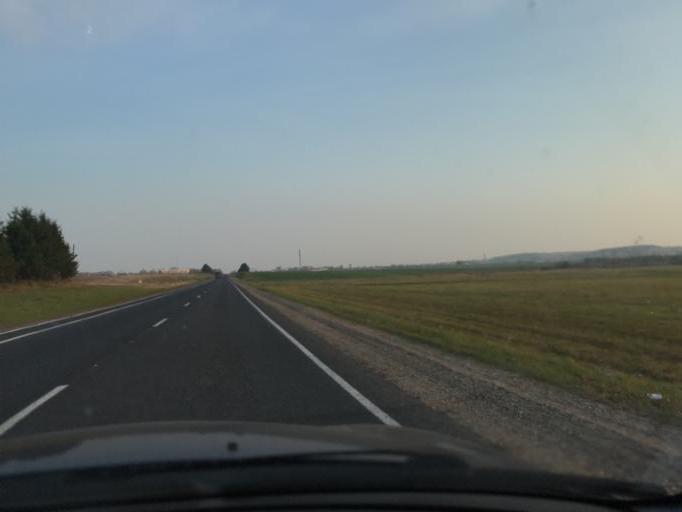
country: BY
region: Grodnenskaya
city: Karelichy
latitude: 53.5838
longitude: 26.1141
